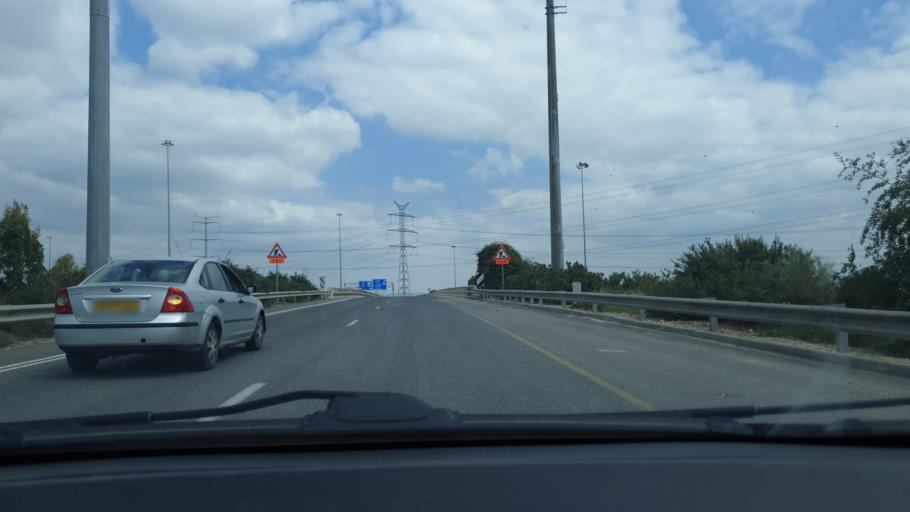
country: IL
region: Central District
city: Ramla
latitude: 31.9091
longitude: 34.8932
